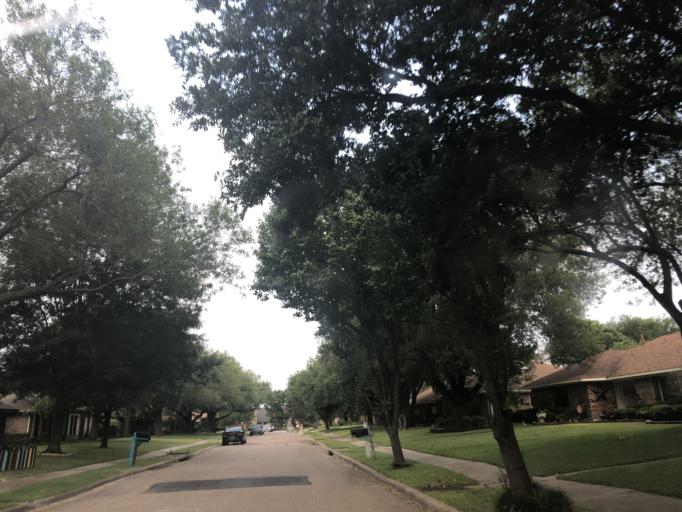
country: US
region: Texas
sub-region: Dallas County
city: Garland
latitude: 32.8463
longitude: -96.6262
